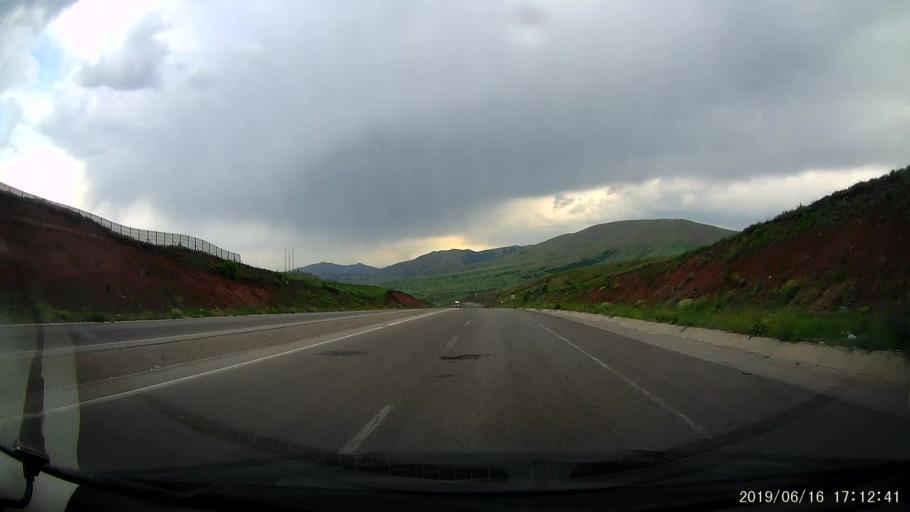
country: TR
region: Erzurum
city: Askale
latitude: 39.8593
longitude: 40.6143
